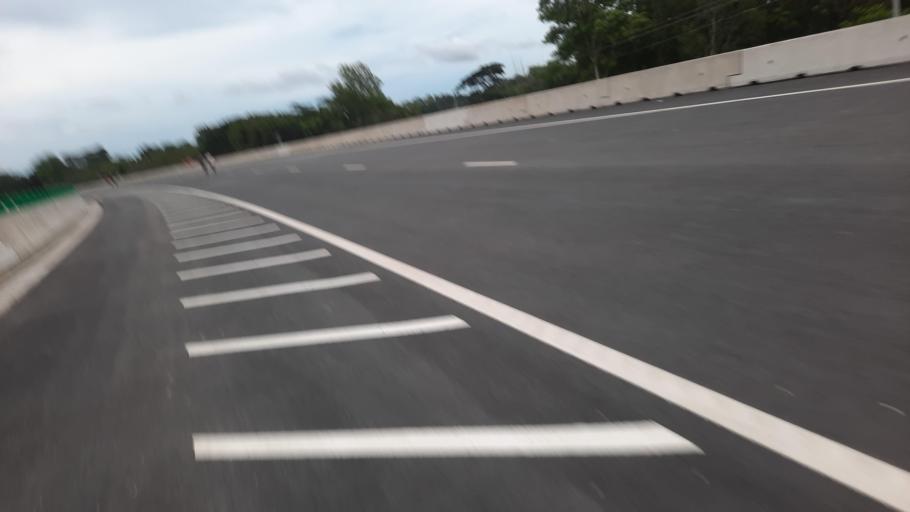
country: BD
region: Khulna
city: Kalia
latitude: 23.1889
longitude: 89.6991
